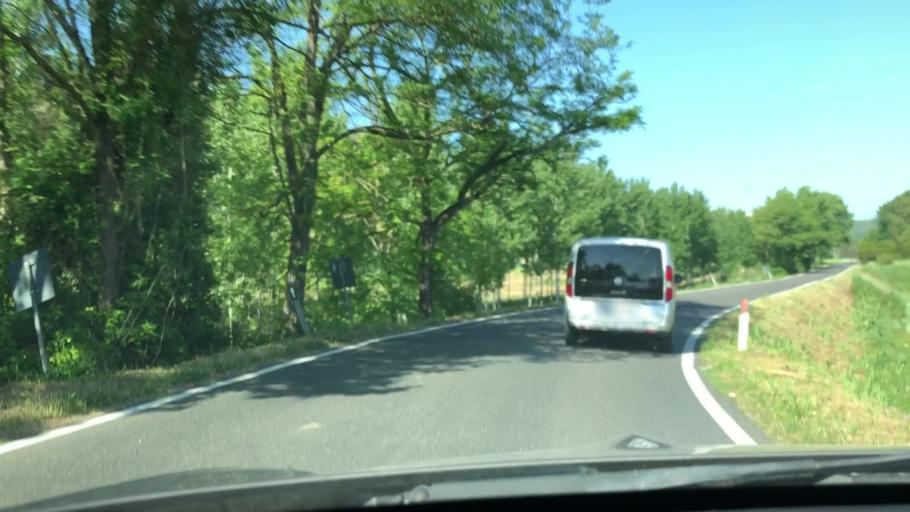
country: IT
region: Tuscany
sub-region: Province of Pisa
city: Capannoli
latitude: 43.5925
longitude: 10.6847
